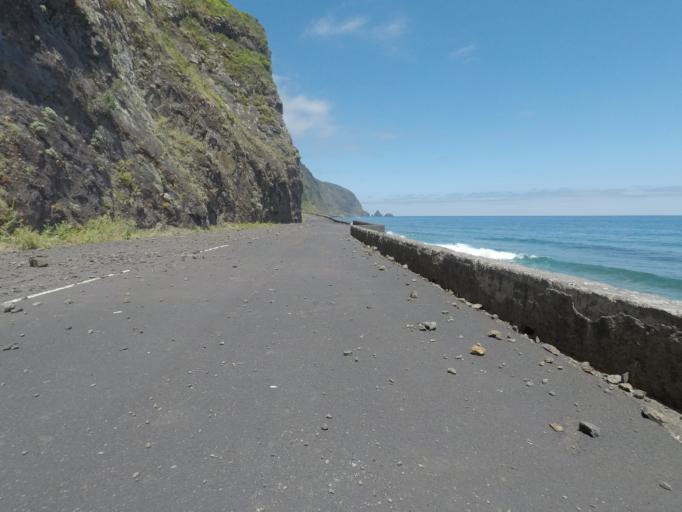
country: PT
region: Madeira
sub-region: Porto Moniz
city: Porto Moniz
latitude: 32.8276
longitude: -17.1255
